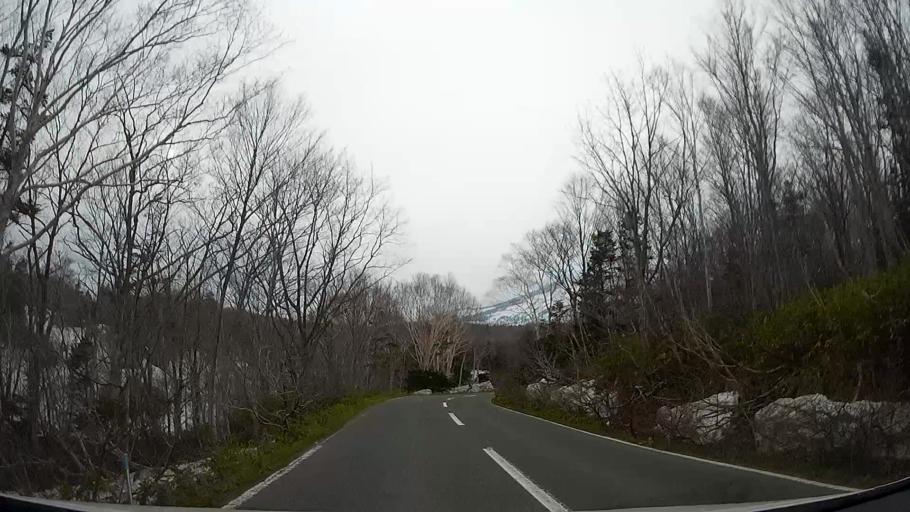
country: JP
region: Aomori
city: Aomori Shi
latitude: 40.6310
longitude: 140.9121
